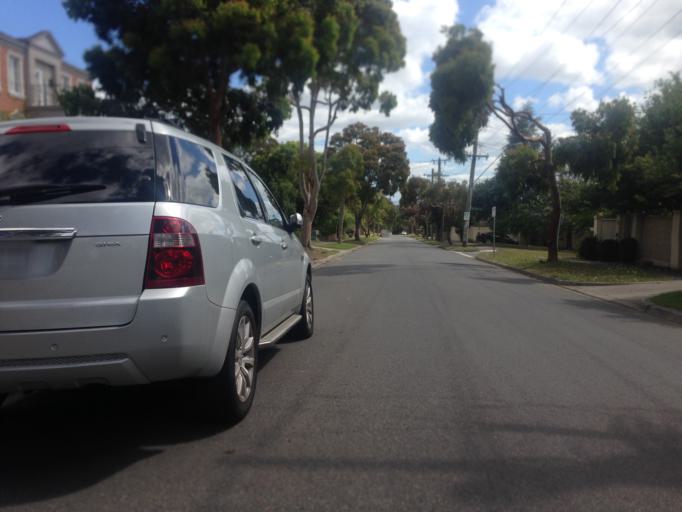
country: AU
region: Victoria
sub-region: Boroondara
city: Balwyn North
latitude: -37.7847
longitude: 145.0833
